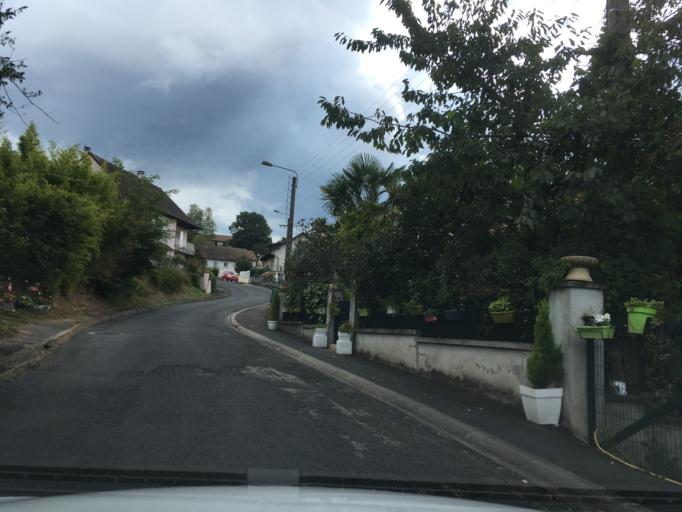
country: FR
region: Limousin
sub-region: Departement de la Correze
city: Brive-la-Gaillarde
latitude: 45.1457
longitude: 1.5378
